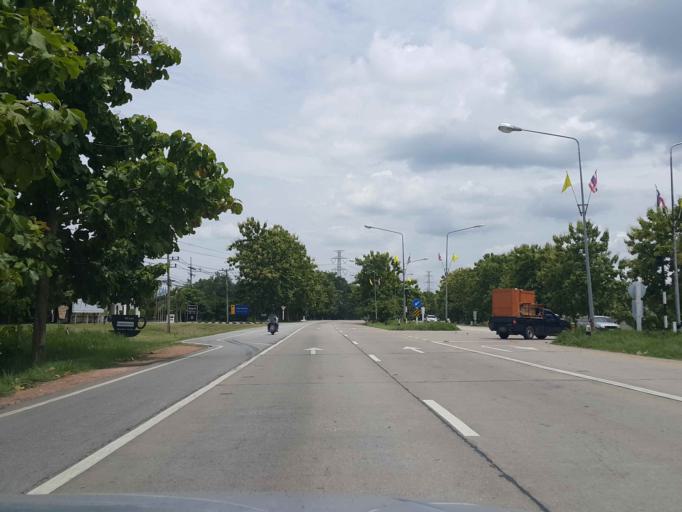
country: TH
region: Lamphun
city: Lamphun
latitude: 18.5386
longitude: 99.0712
